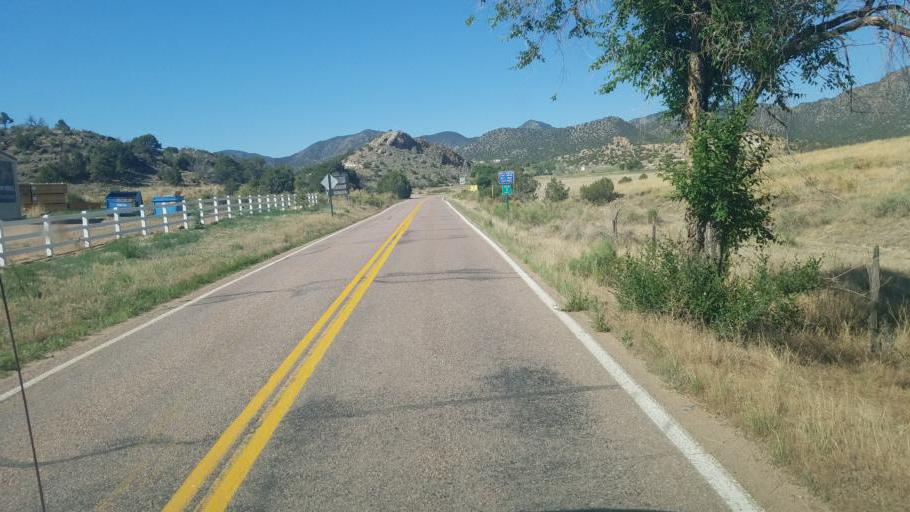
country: US
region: Colorado
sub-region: Fremont County
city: Canon City
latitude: 38.4850
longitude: -105.3758
